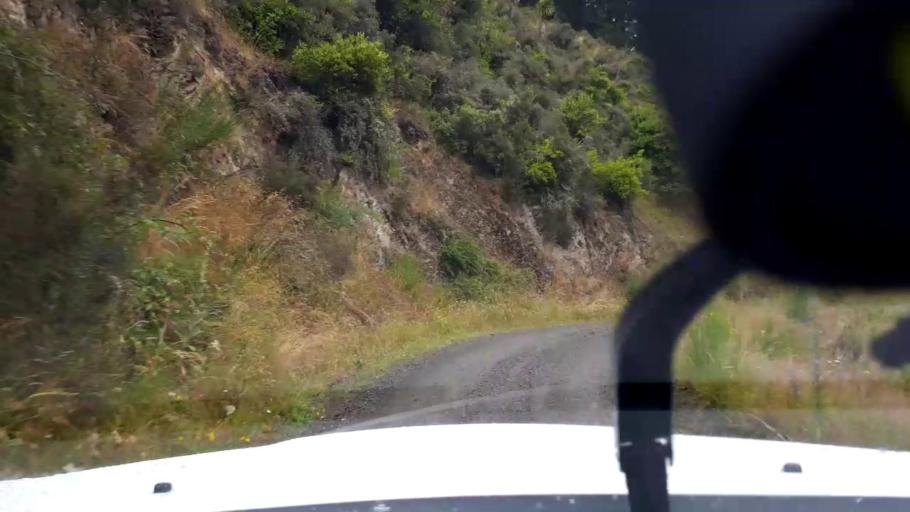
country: NZ
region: Canterbury
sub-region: Timaru District
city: Pleasant Point
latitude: -44.0367
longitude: 171.0088
